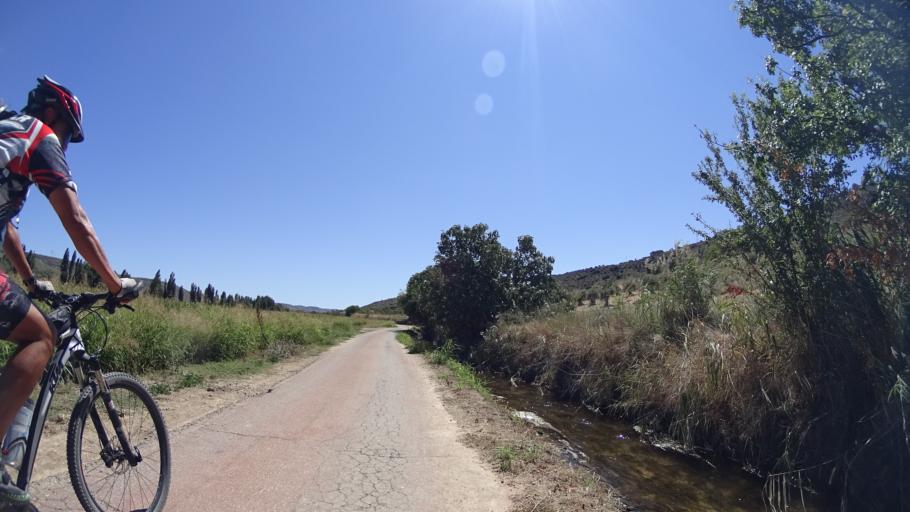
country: ES
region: Madrid
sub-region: Provincia de Madrid
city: Tielmes
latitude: 40.2425
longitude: -3.2908
